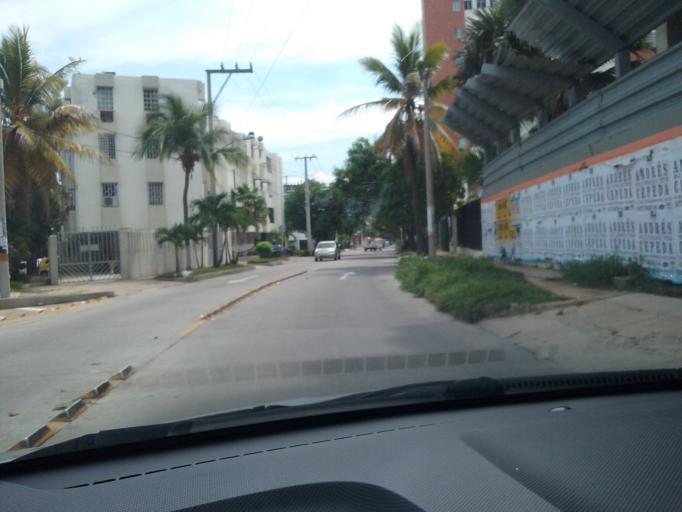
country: CO
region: Atlantico
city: Barranquilla
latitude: 11.0113
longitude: -74.8073
